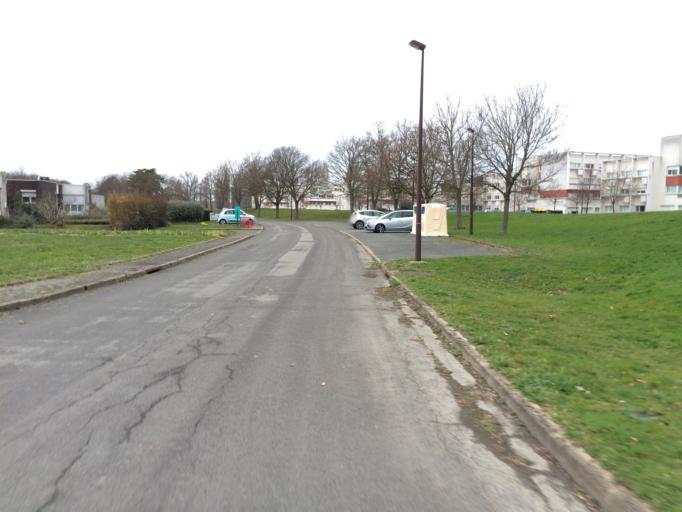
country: FR
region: Ile-de-France
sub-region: Departement de l'Essonne
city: Villebon-sur-Yvette
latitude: 48.7096
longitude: 2.2155
